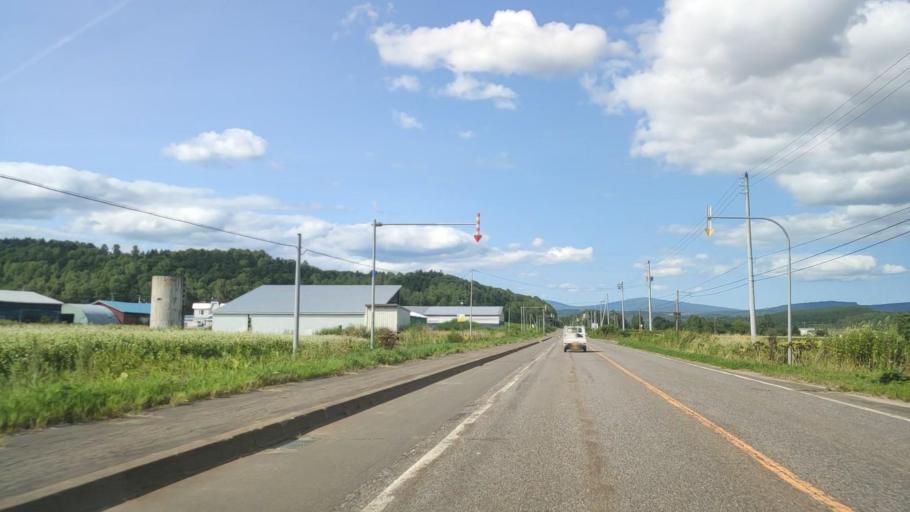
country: JP
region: Hokkaido
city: Nayoro
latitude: 44.4002
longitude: 142.3959
